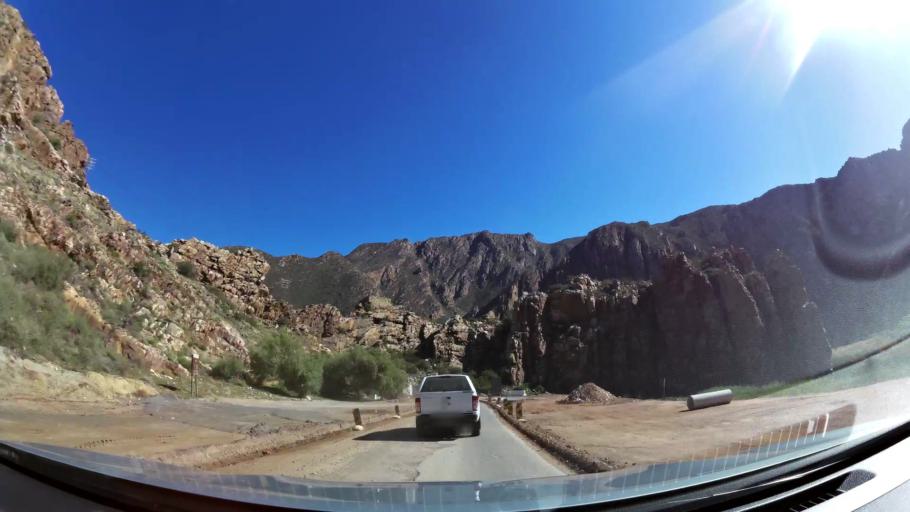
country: ZA
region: Western Cape
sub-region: Cape Winelands District Municipality
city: Ashton
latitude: -33.8031
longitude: 20.0958
